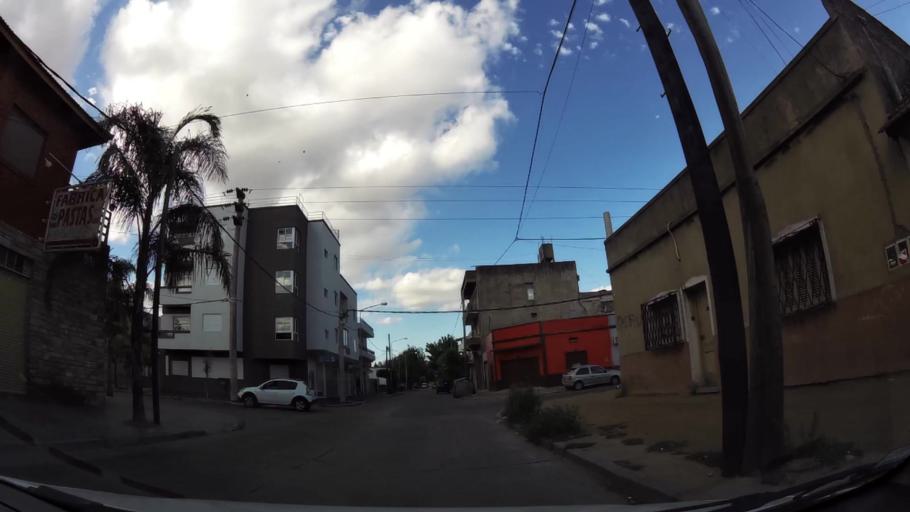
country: AR
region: Buenos Aires
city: San Justo
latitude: -34.6730
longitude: -58.5732
